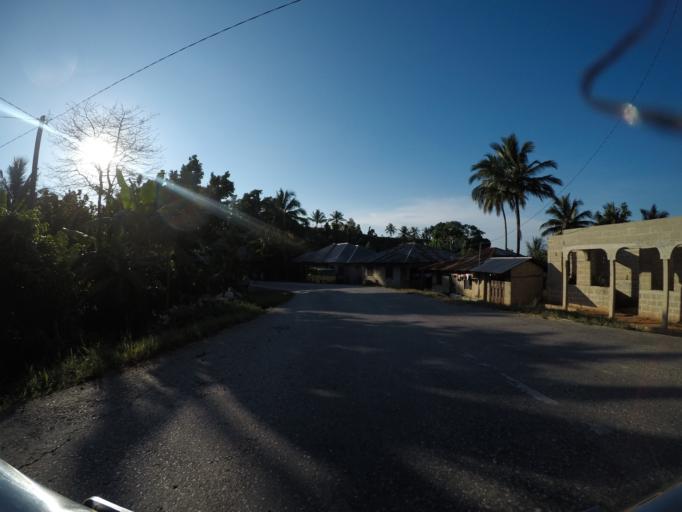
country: TZ
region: Pemba South
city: Mtambile
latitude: -5.3793
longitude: 39.6850
